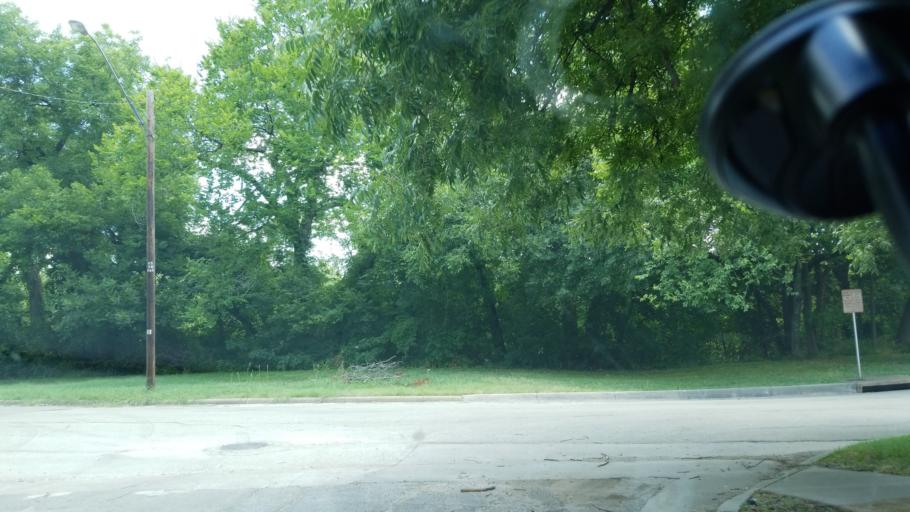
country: US
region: Texas
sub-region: Dallas County
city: Cockrell Hill
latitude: 32.6977
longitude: -96.8466
